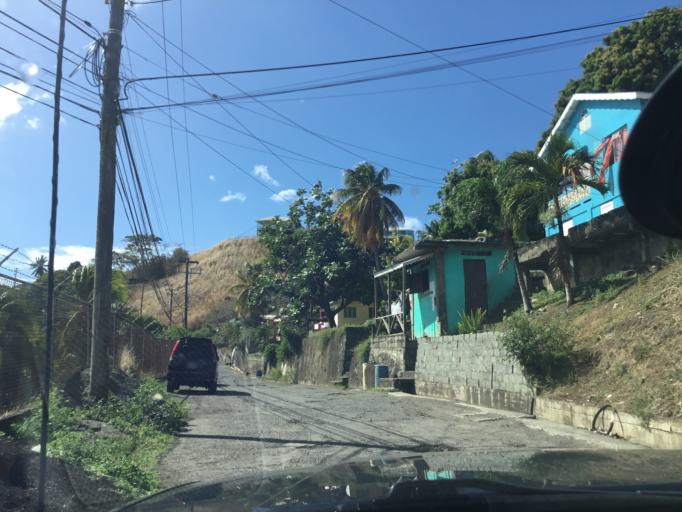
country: VC
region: Saint George
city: Kingstown Park
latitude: 13.1727
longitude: -61.2480
